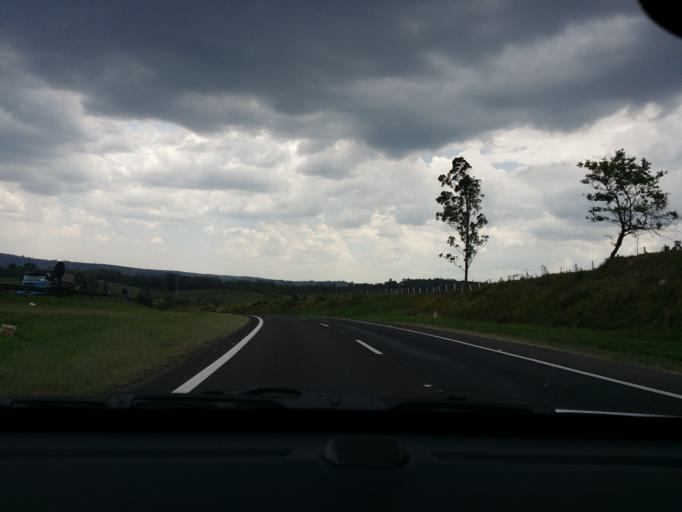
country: BR
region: Sao Paulo
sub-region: Rio Claro
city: Rio Claro
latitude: -22.3219
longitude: -47.6566
